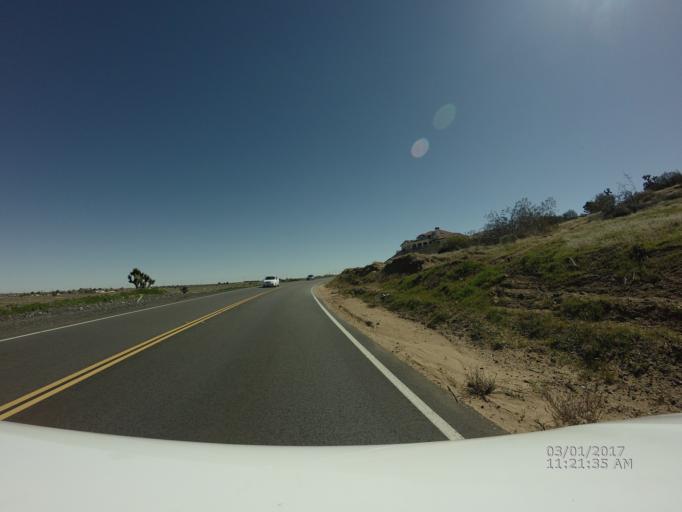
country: US
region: California
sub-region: Los Angeles County
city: Quartz Hill
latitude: 34.6470
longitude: -118.2000
